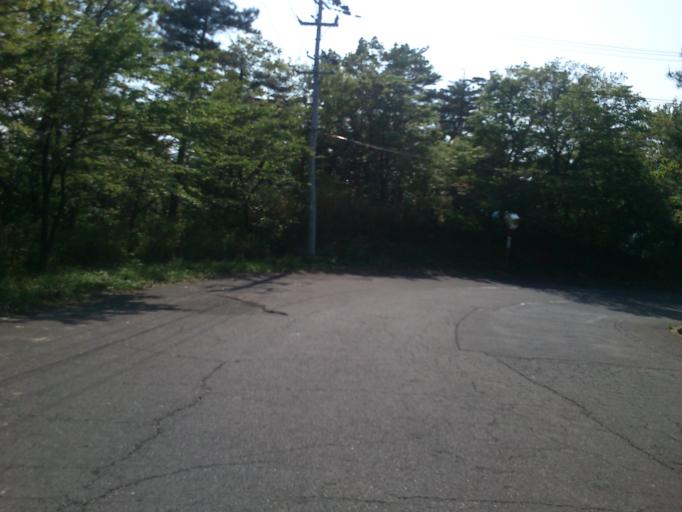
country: JP
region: Kyoto
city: Miyazu
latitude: 35.7323
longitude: 135.1773
